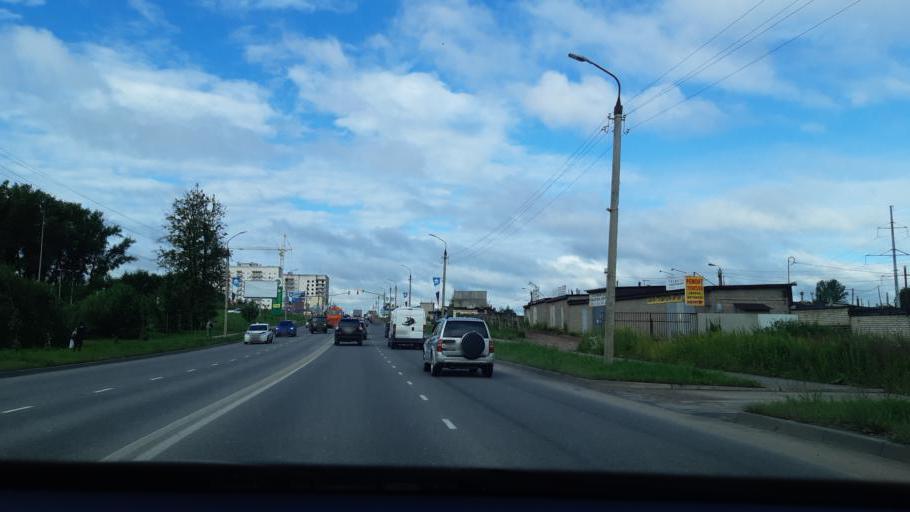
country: RU
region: Smolensk
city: Smolensk
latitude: 54.7599
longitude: 32.0821
